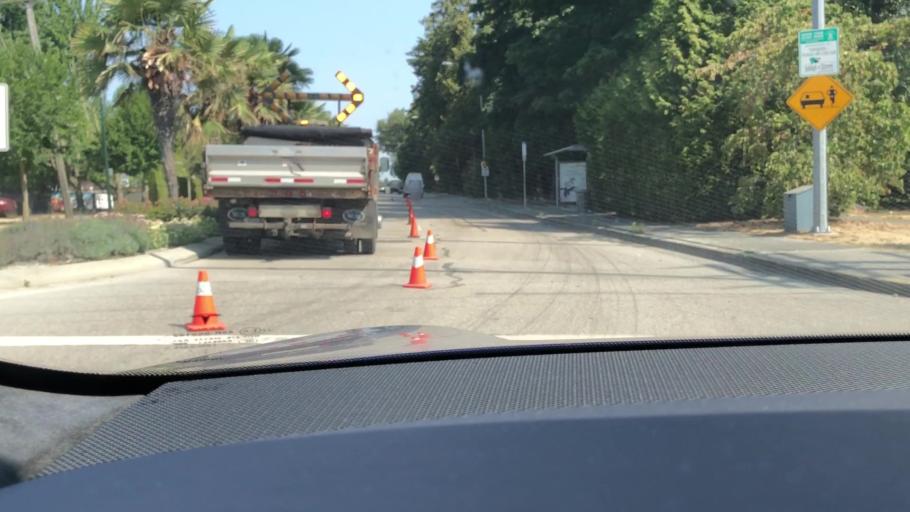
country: US
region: Washington
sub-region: Whatcom County
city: Point Roberts
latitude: 49.0139
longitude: -123.0685
